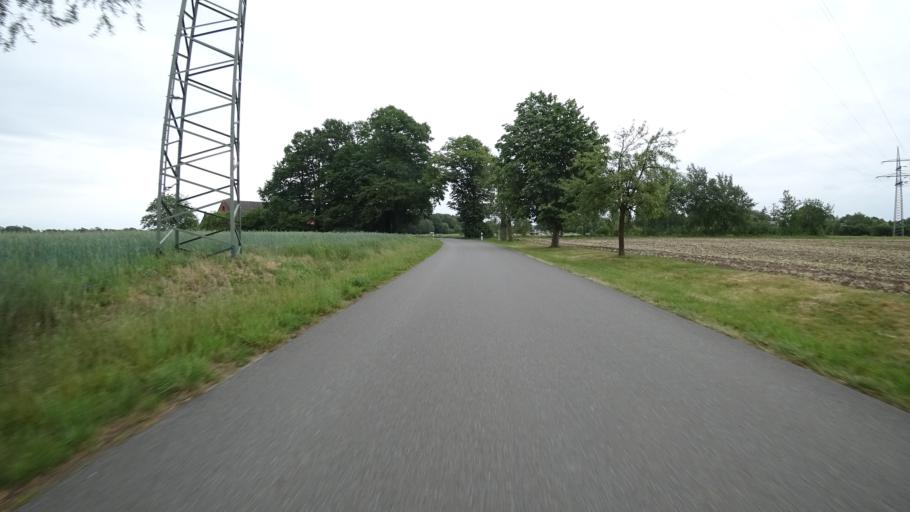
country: DE
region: North Rhine-Westphalia
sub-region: Regierungsbezirk Detmold
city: Rheda-Wiedenbruck
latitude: 51.8457
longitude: 8.3356
